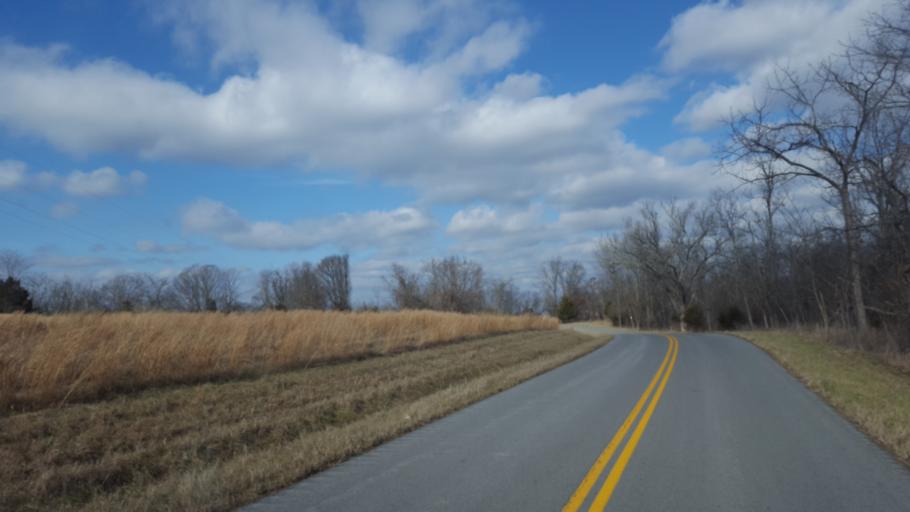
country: US
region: Kentucky
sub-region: Franklin County
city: Frankfort
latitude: 38.3715
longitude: -84.9441
